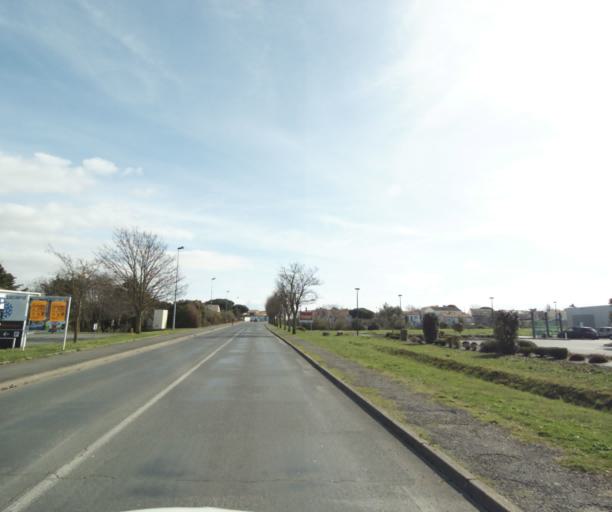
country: FR
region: Poitou-Charentes
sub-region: Departement de la Charente-Maritime
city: La Rochelle
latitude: 46.1733
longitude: -1.1659
